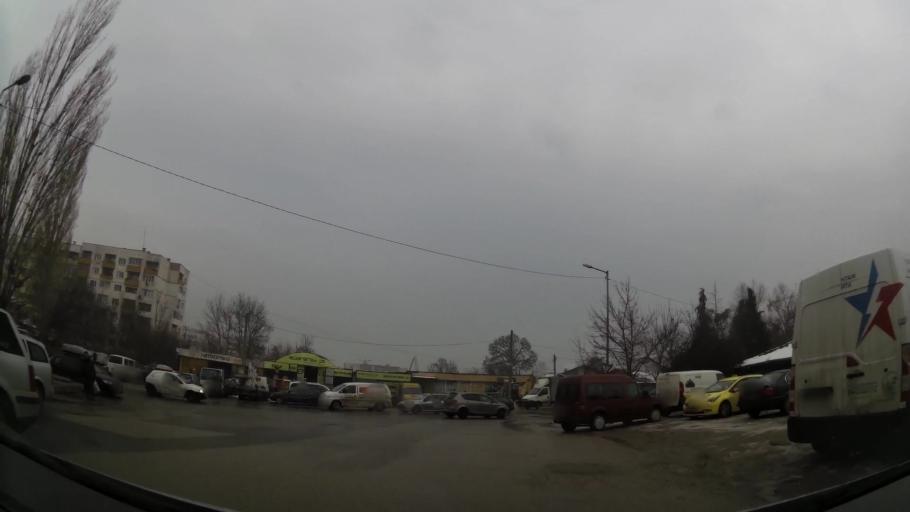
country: BG
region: Sofia-Capital
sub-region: Stolichna Obshtina
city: Sofia
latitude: 42.6849
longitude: 23.2555
